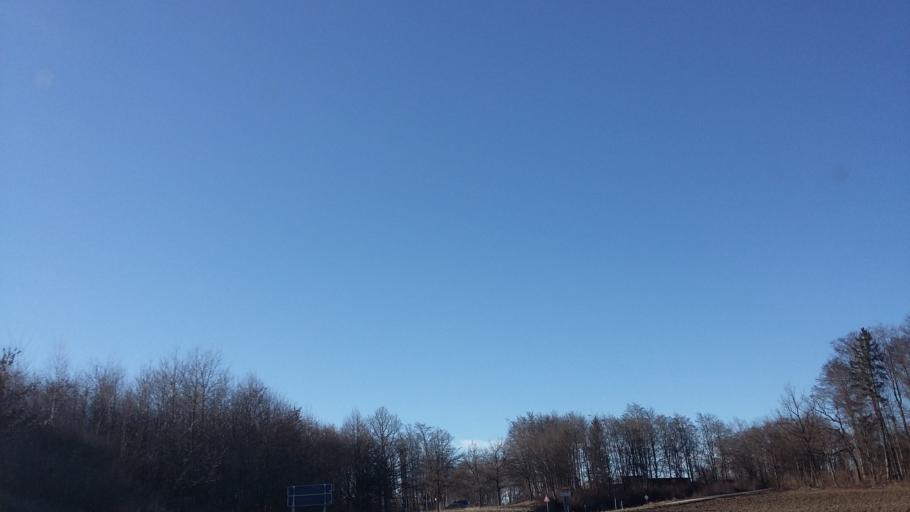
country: DE
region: Bavaria
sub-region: Upper Bavaria
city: Pocking
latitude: 47.9830
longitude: 11.3115
